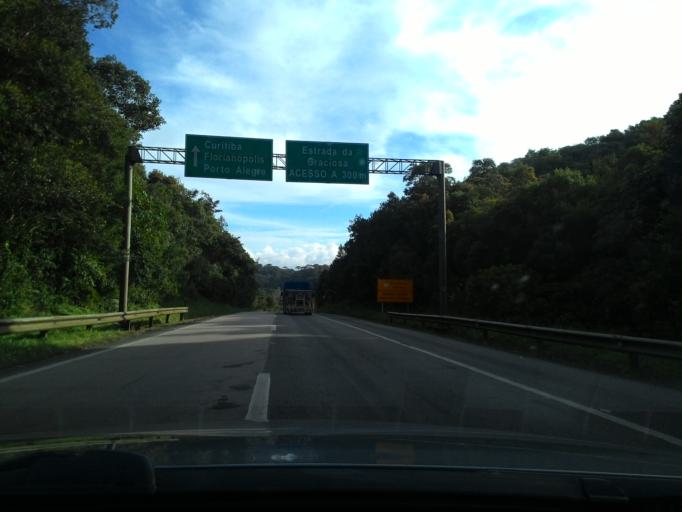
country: BR
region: Parana
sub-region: Campina Grande Do Sul
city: Campina Grande do Sul
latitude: -25.3009
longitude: -48.9424
